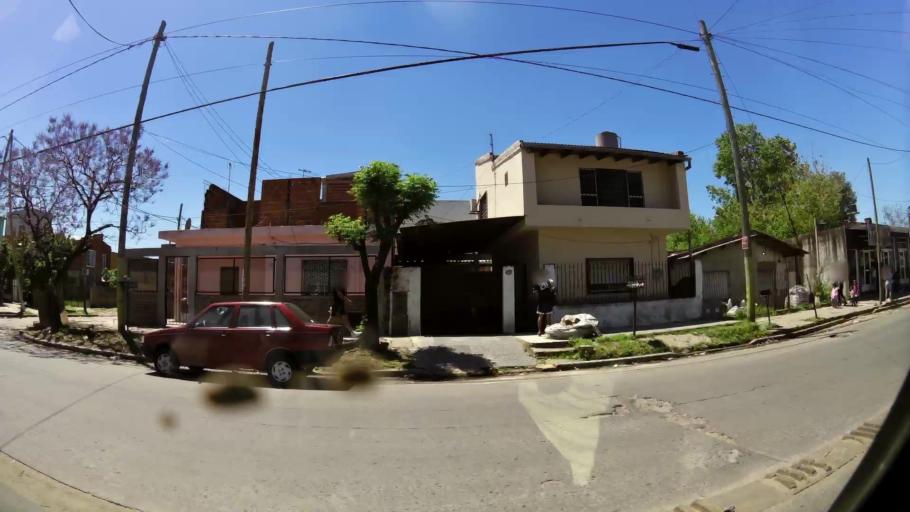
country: AR
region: Buenos Aires
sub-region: Partido de Quilmes
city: Quilmes
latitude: -34.7202
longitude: -58.3183
